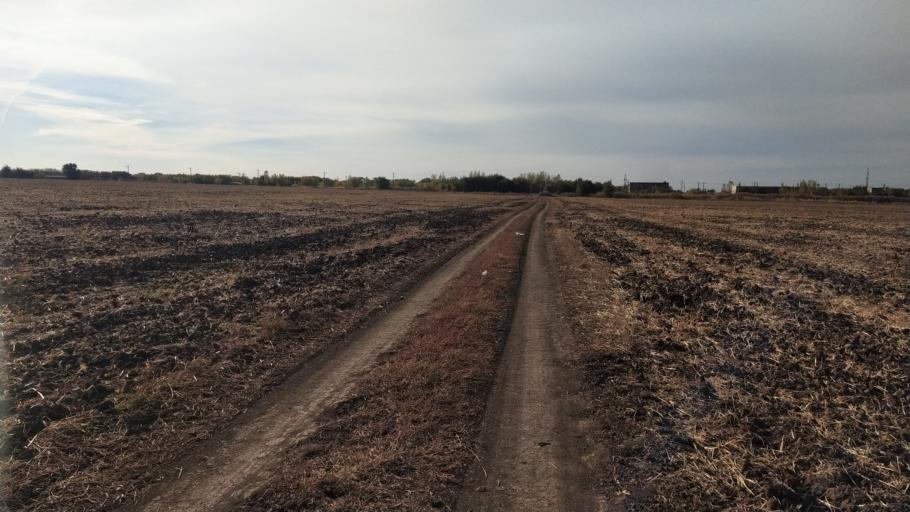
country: RU
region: Rostov
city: Bataysk
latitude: 47.1141
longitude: 39.7198
